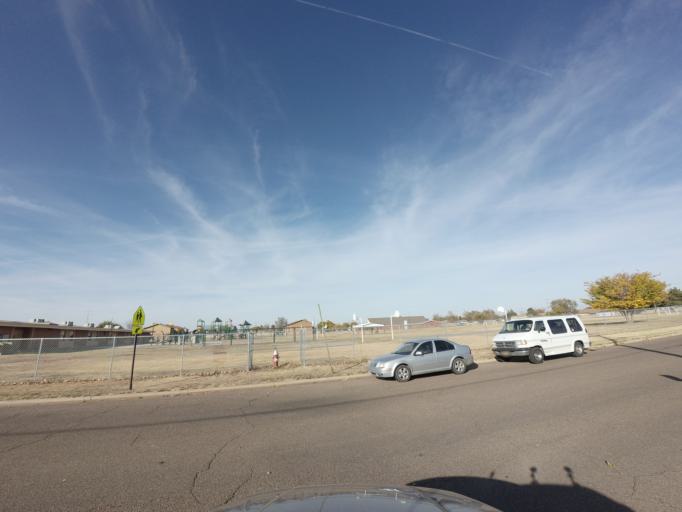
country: US
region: New Mexico
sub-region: Curry County
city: Clovis
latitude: 34.4265
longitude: -103.2244
